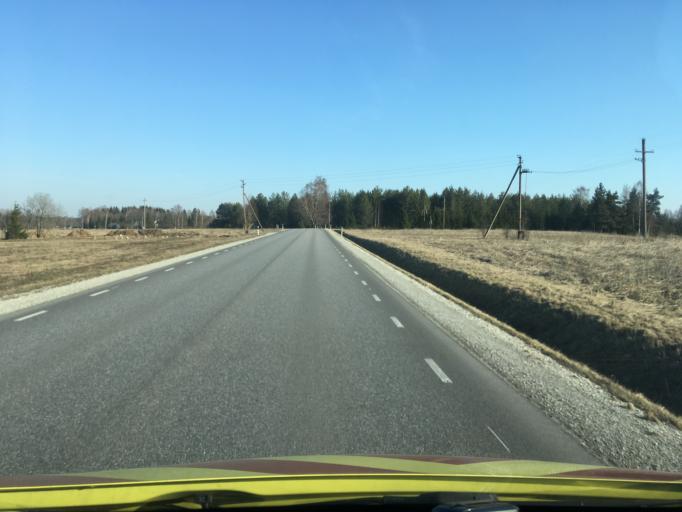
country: EE
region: Raplamaa
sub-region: Rapla vald
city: Rapla
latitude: 59.0052
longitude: 24.8425
